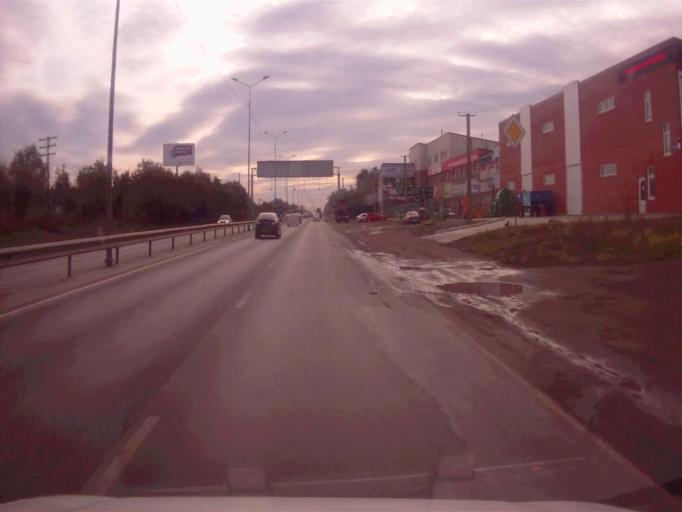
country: RU
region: Chelyabinsk
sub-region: Gorod Chelyabinsk
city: Chelyabinsk
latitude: 55.1100
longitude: 61.4094
